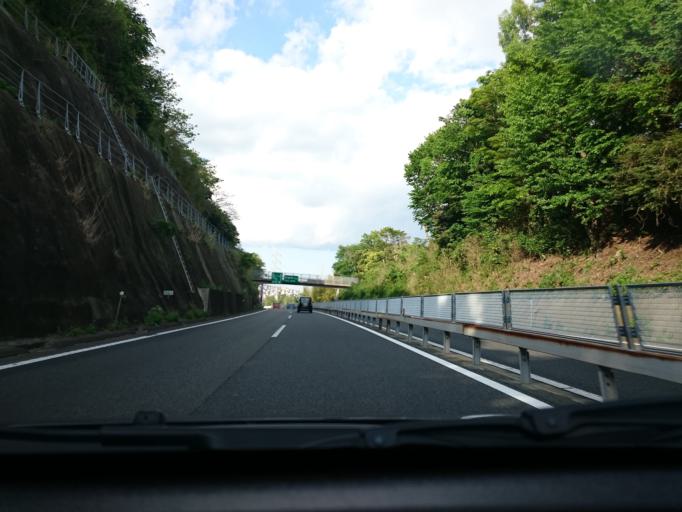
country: JP
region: Kanagawa
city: Oiso
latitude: 35.3296
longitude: 139.2901
